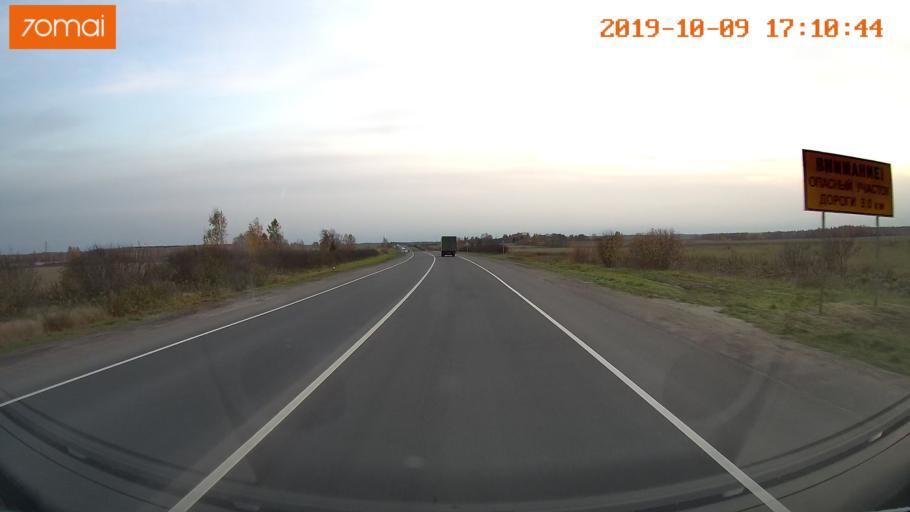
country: RU
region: Ivanovo
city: Privolzhsk
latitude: 57.3518
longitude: 41.2552
